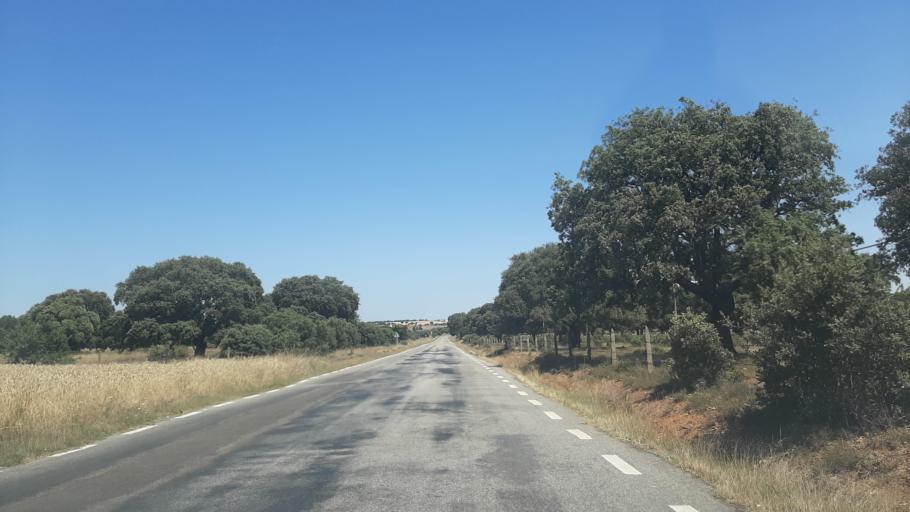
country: ES
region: Castille and Leon
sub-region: Provincia de Salamanca
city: Cabrillas
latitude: 40.7268
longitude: -6.1760
